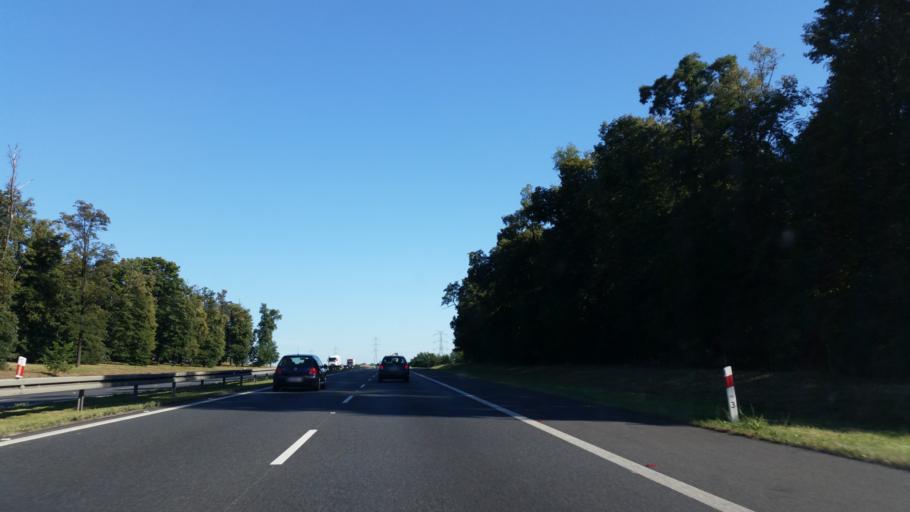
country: PL
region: Opole Voivodeship
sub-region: Powiat brzeski
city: Skarbimierz Osiedle
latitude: 50.8004
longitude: 17.3226
